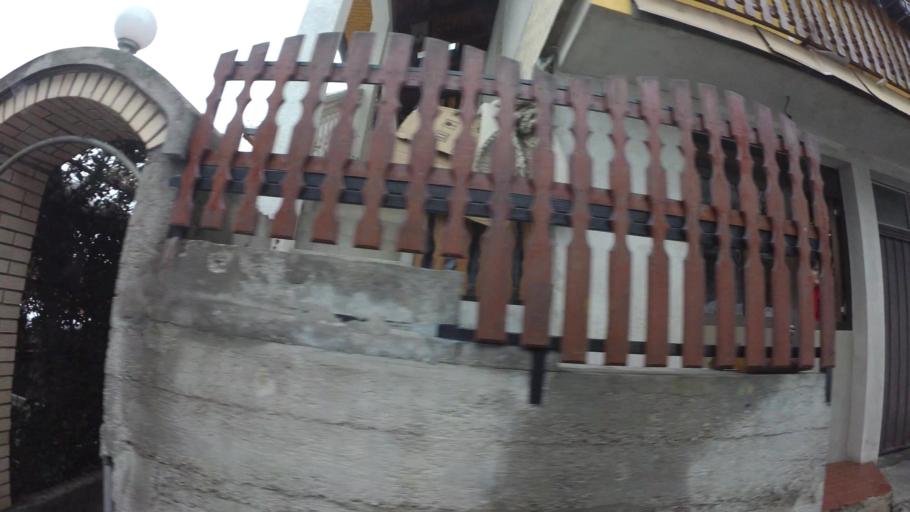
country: BA
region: Federation of Bosnia and Herzegovina
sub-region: Kanton Sarajevo
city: Sarajevo
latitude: 43.8564
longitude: 18.3479
